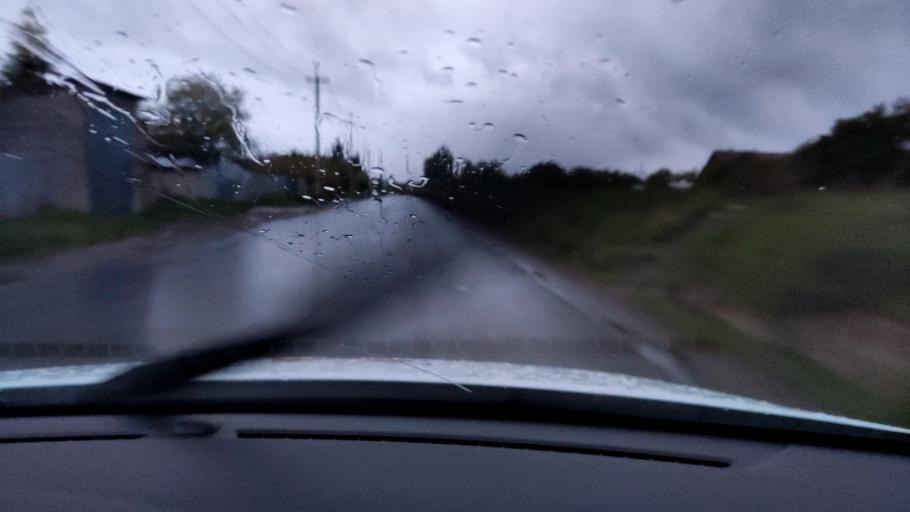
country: RU
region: Tatarstan
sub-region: Gorod Kazan'
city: Kazan
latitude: 55.7228
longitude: 49.1140
